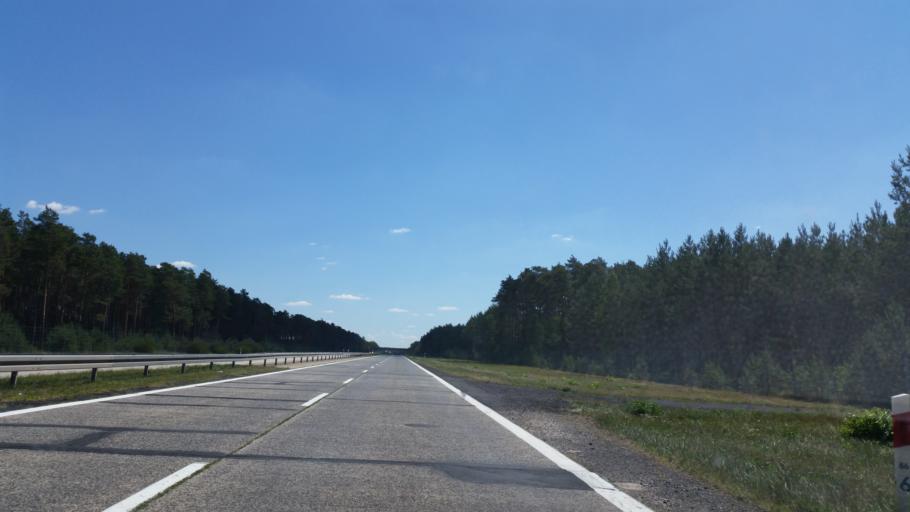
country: PL
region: Lower Silesian Voivodeship
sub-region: Powiat boleslawiecki
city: Boleslawiec
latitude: 51.3821
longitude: 15.5479
